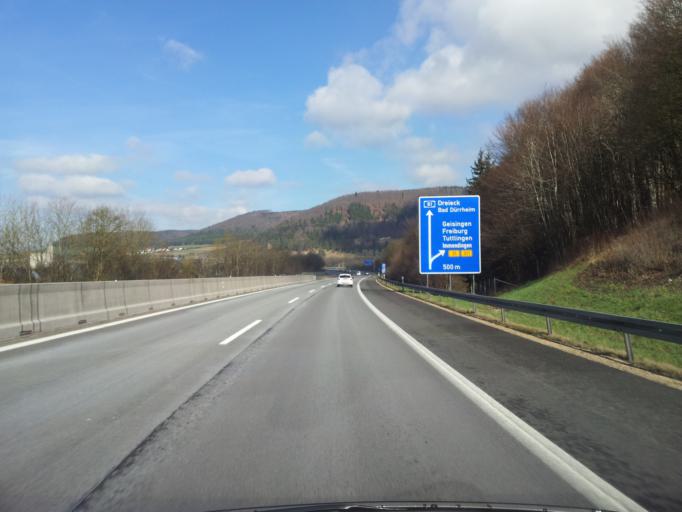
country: DE
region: Baden-Wuerttemberg
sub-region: Freiburg Region
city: Geisingen
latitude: 47.9148
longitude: 8.6801
